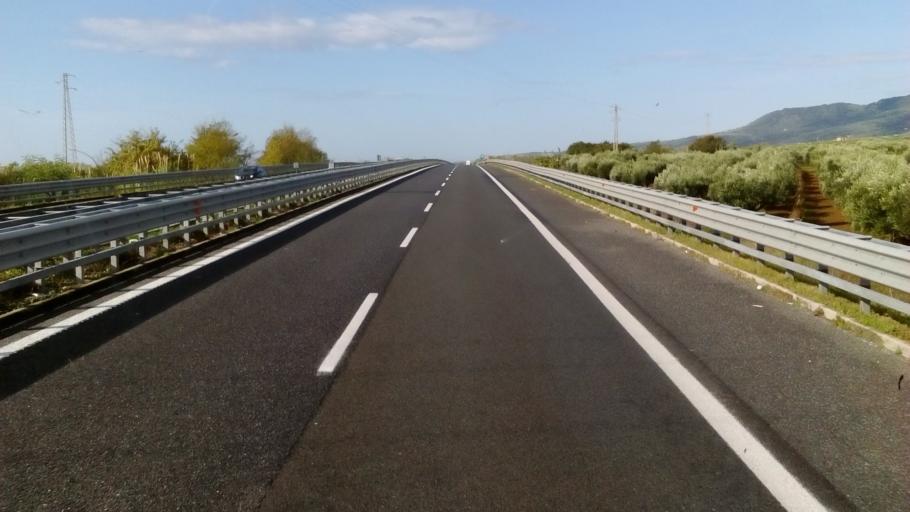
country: IT
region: Calabria
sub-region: Provincia di Catanzaro
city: Santa Eufemia Lamezia
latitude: 38.9255
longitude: 16.2527
